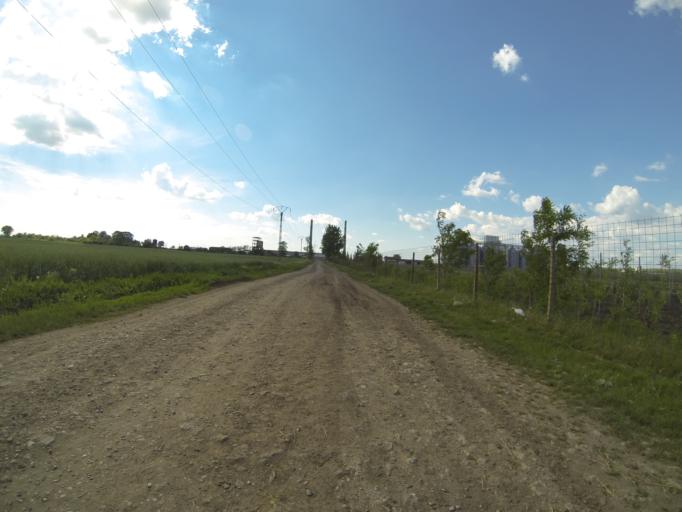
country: RO
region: Dolj
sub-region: Comuna Segarcea
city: Segarcea
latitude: 44.0812
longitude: 23.7305
